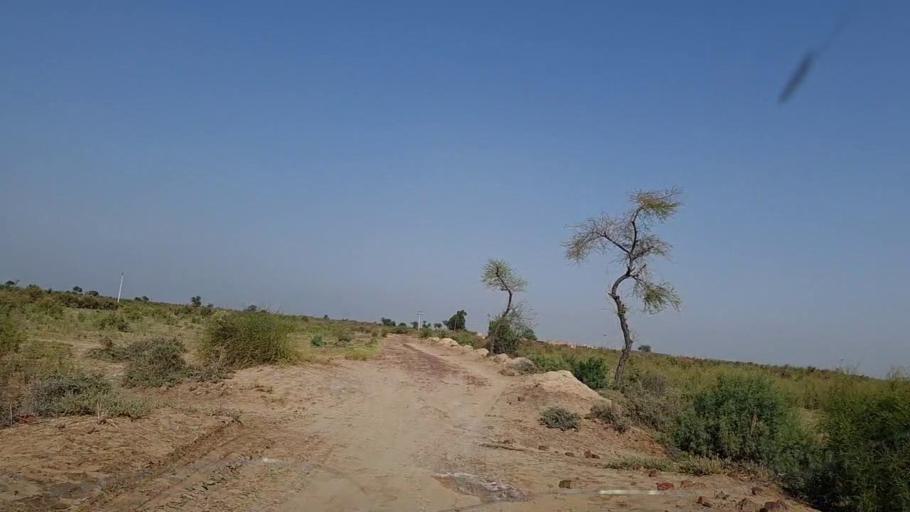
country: PK
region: Sindh
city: Khanpur
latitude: 27.6756
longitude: 69.3714
